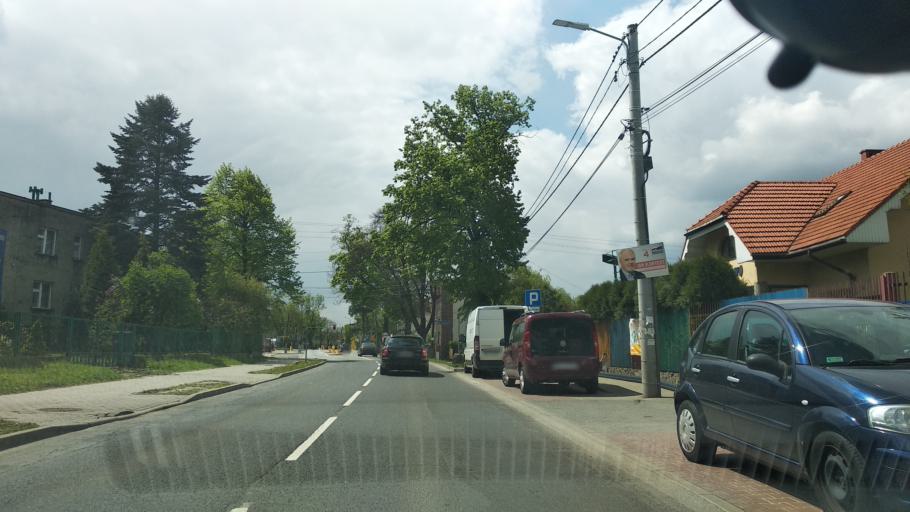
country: PL
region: Silesian Voivodeship
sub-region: Swietochlowice
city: Swietochlowice
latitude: 50.2309
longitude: 18.9512
